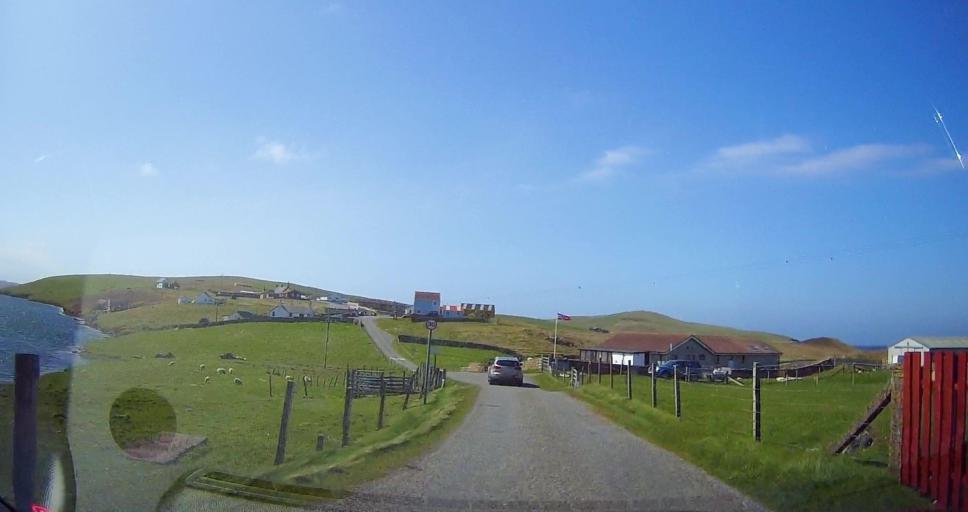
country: GB
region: Scotland
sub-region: Shetland Islands
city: Sandwick
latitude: 60.0824
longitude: -1.3327
